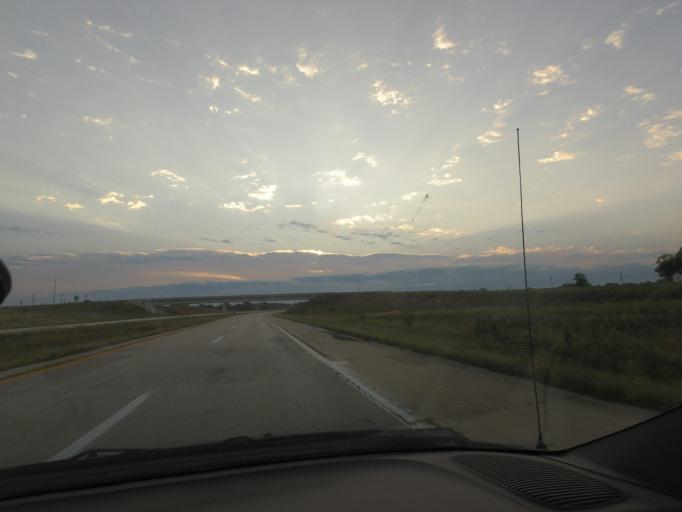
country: US
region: Missouri
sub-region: Macon County
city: Macon
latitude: 39.7520
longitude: -92.2600
